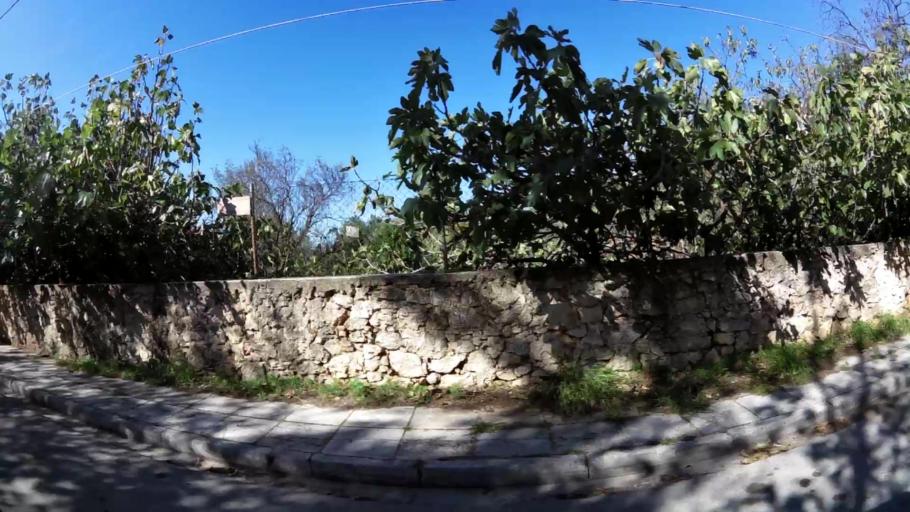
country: GR
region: Attica
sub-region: Nomarchia Athinas
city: Kifisia
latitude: 38.0898
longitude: 23.7926
